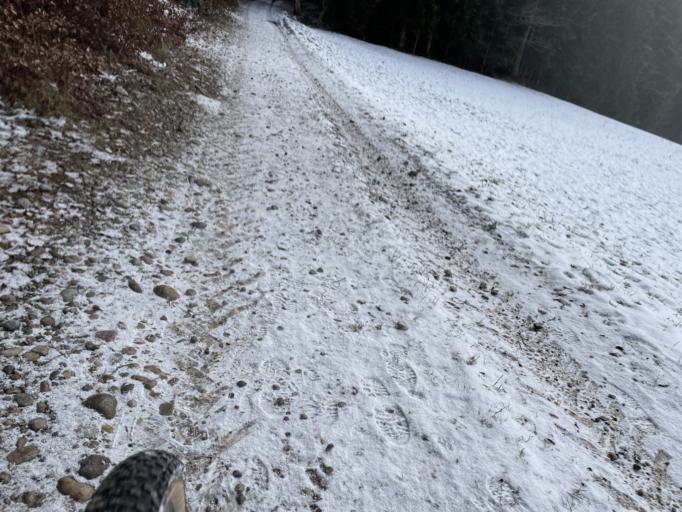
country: CH
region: Lucerne
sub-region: Entlebuch District
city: Oberdiessbach
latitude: 46.8495
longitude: 7.6086
